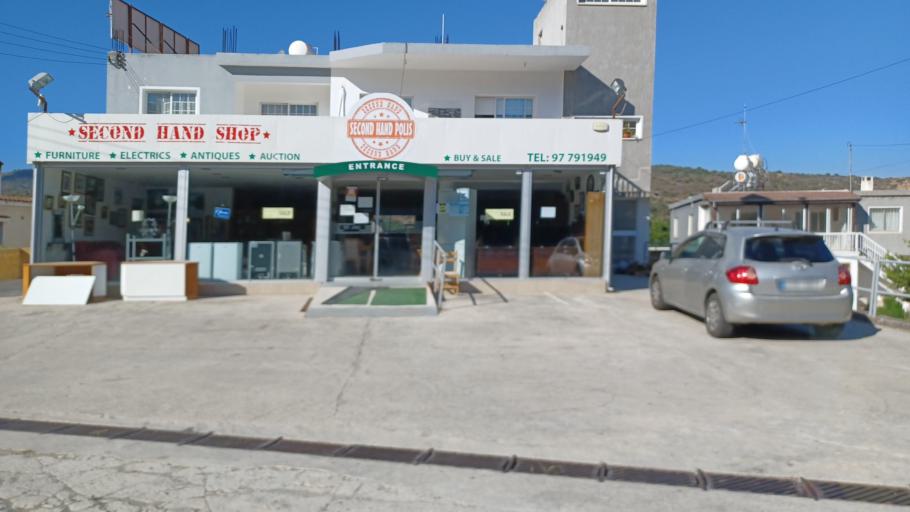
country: CY
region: Pafos
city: Polis
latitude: 34.9848
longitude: 32.4529
